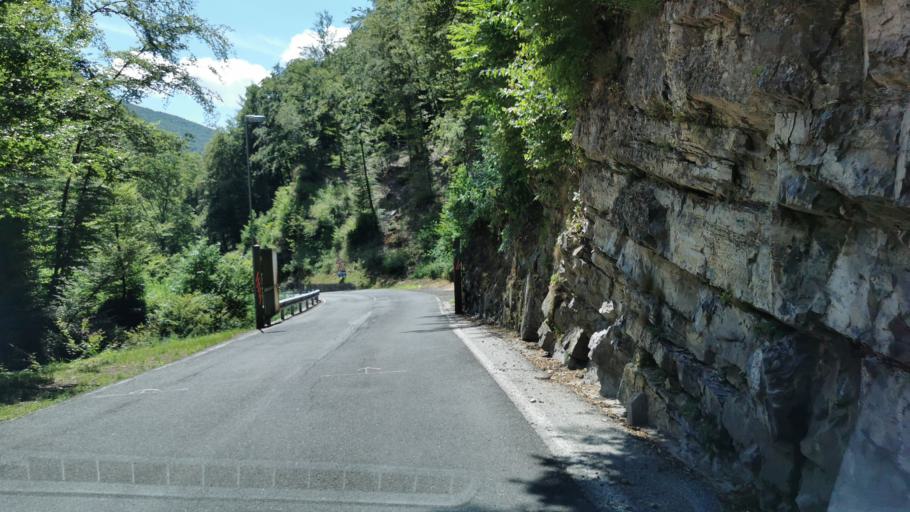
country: IT
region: Lombardy
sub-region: Provincia di Como
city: Lanzo d'Intelvi
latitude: 45.9663
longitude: 9.0171
